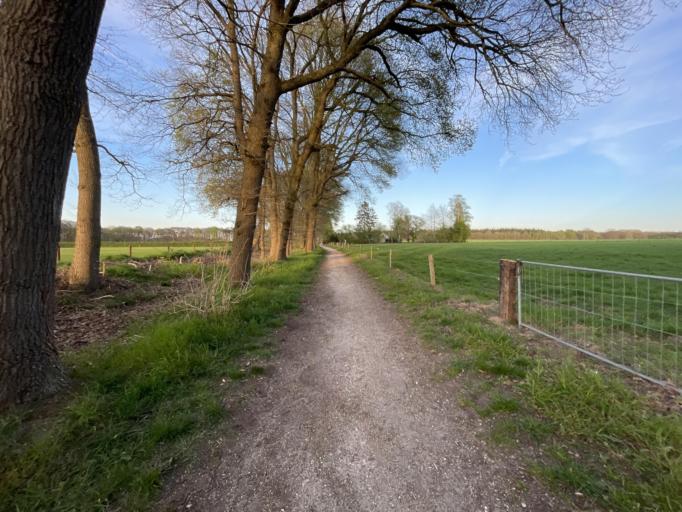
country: NL
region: Gelderland
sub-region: Gemeente Groesbeek
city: Berg en Dal
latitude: 51.8067
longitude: 5.9200
